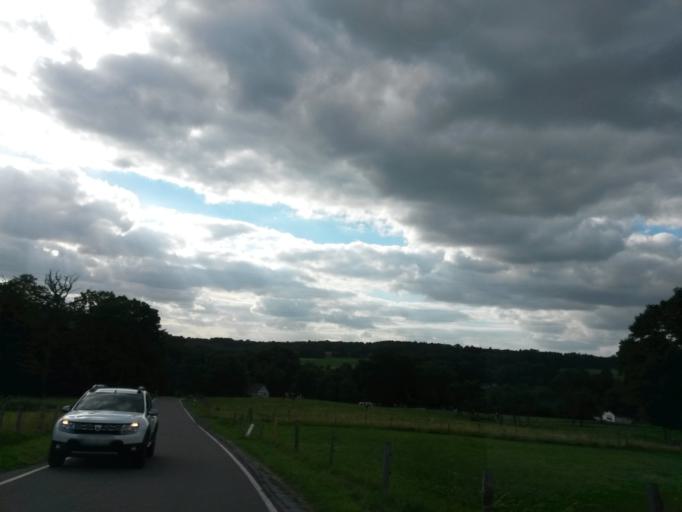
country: DE
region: North Rhine-Westphalia
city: Waldbrol
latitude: 50.9094
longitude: 7.6301
